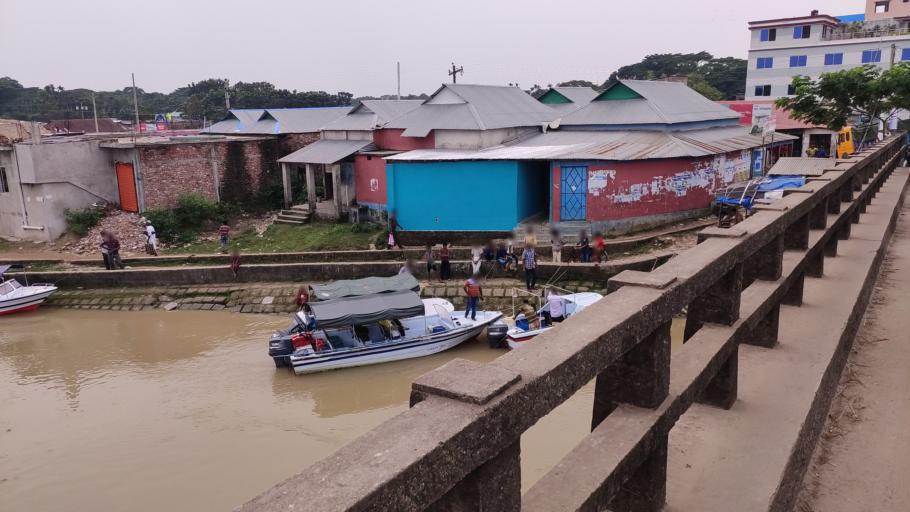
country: BD
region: Dhaka
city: Netrakona
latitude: 24.7167
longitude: 90.9514
